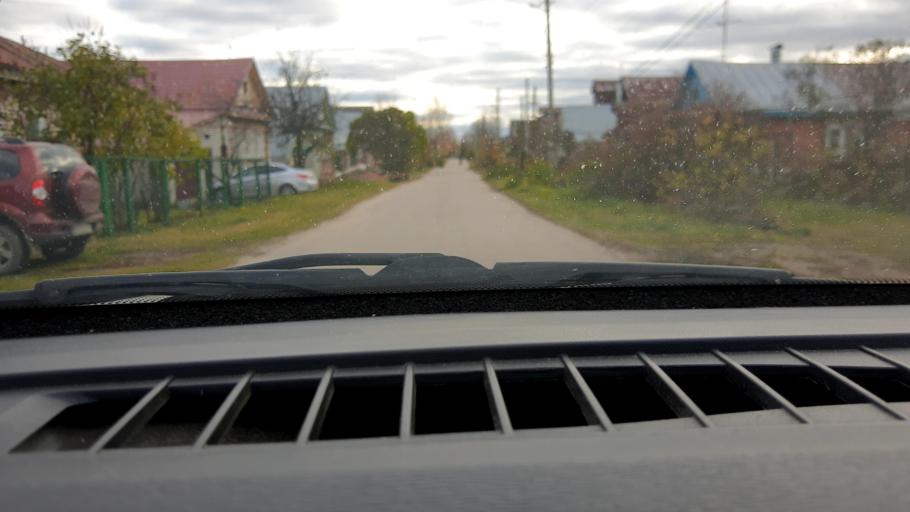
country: RU
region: Nizjnij Novgorod
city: Afonino
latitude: 56.2763
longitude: 44.1059
